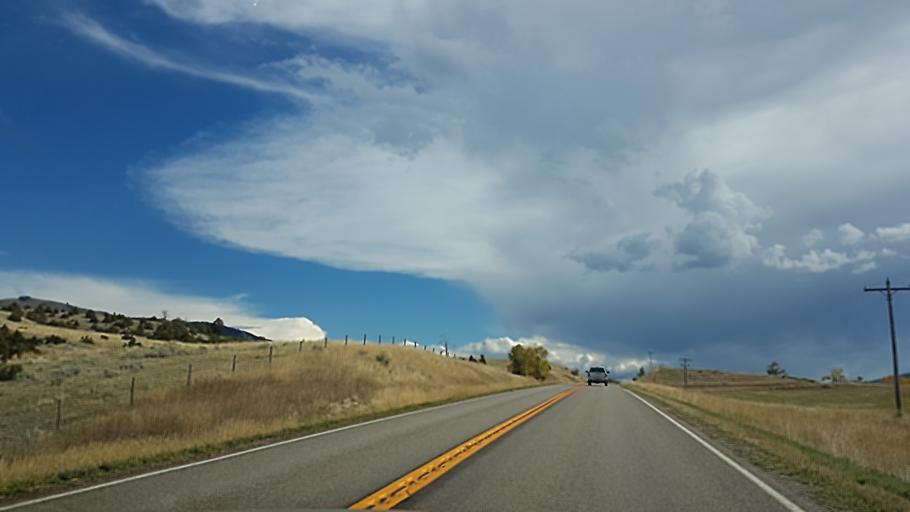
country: US
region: Montana
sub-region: Jefferson County
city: Whitehall
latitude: 45.8005
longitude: -111.9232
